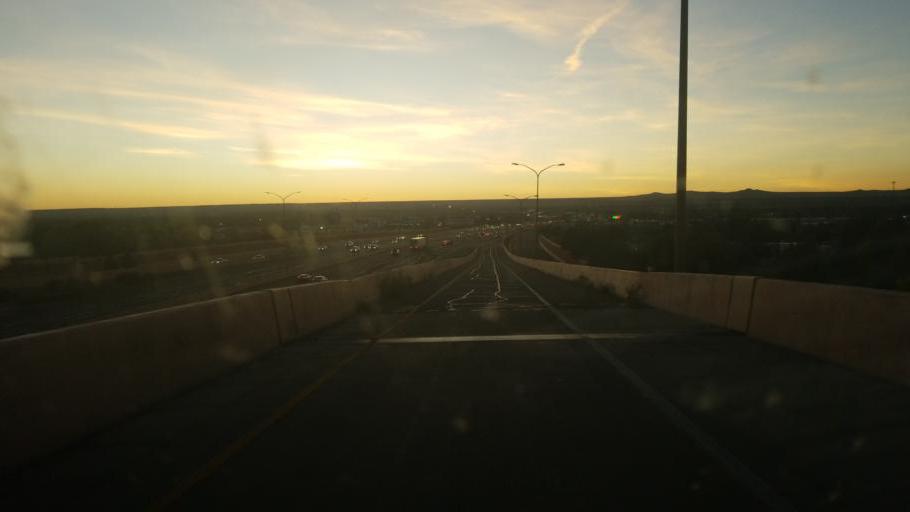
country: US
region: New Mexico
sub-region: Bernalillo County
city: Albuquerque
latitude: 35.1055
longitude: -106.6339
